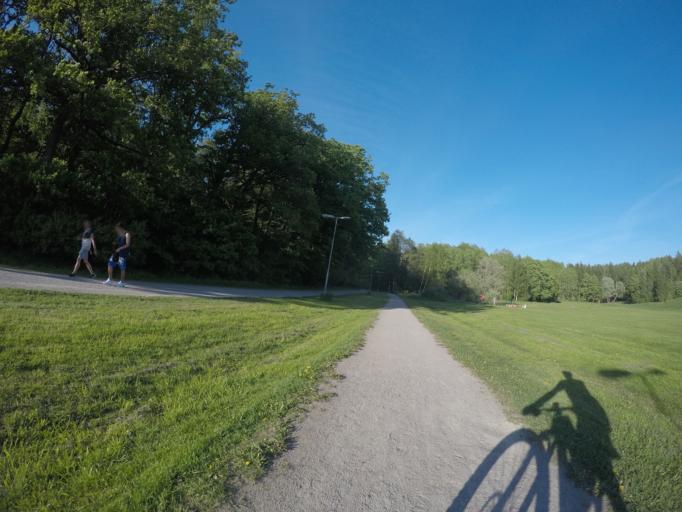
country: SE
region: Soedermanland
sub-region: Eskilstuna Kommun
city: Eskilstuna
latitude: 59.3501
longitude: 16.5122
